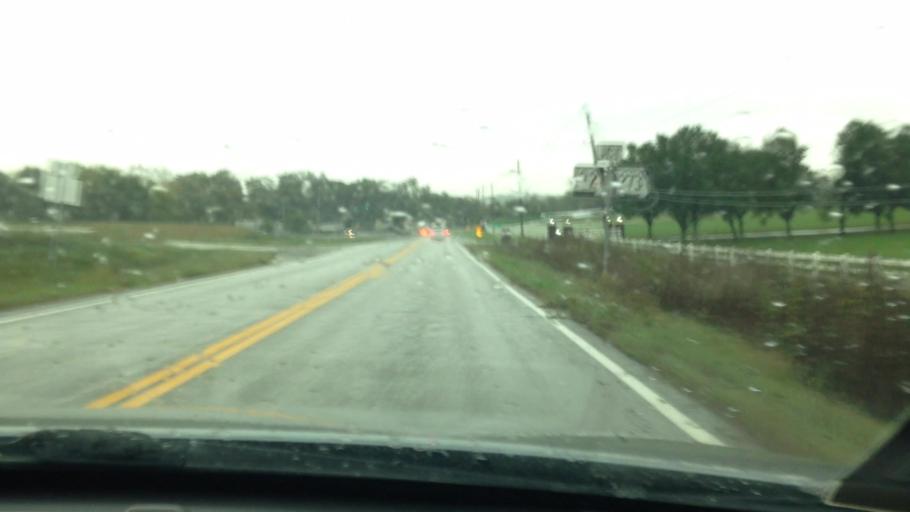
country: US
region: Missouri
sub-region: Platte County
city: Platte City
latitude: 39.3788
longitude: -94.7987
